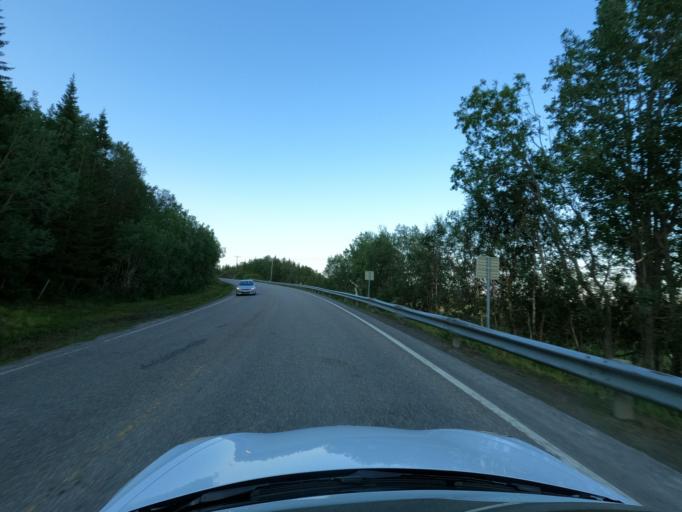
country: NO
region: Troms
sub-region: Harstad
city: Harstad
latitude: 68.7214
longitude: 16.5300
